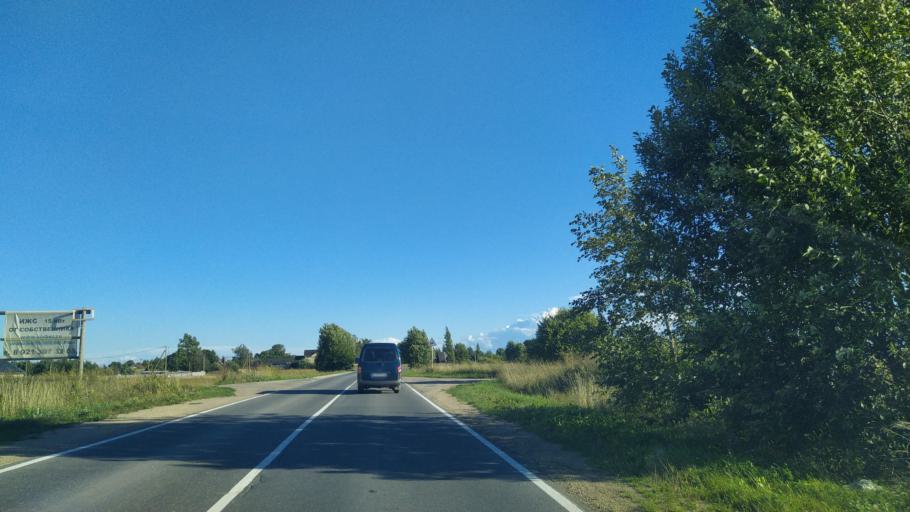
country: RU
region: Leningrad
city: Siverskiy
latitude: 59.3351
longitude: 30.0302
